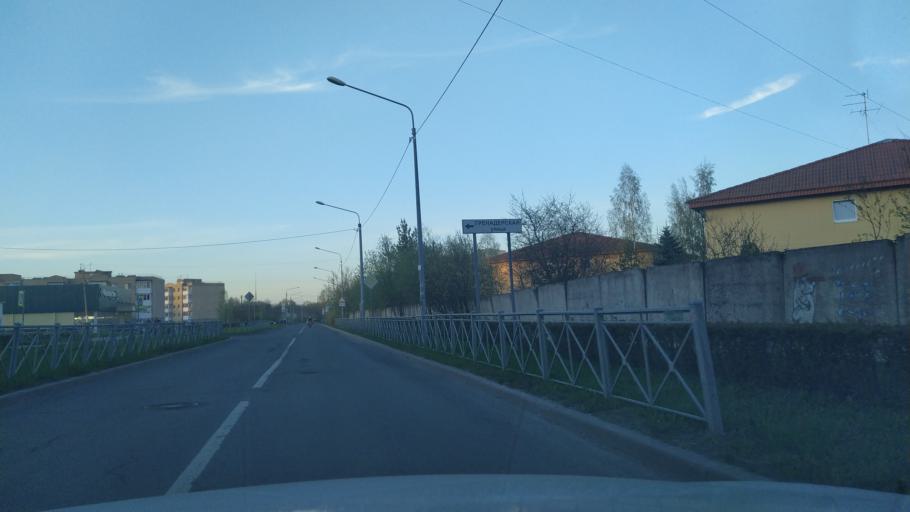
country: RU
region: St.-Petersburg
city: Pushkin
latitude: 59.7024
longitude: 30.3836
